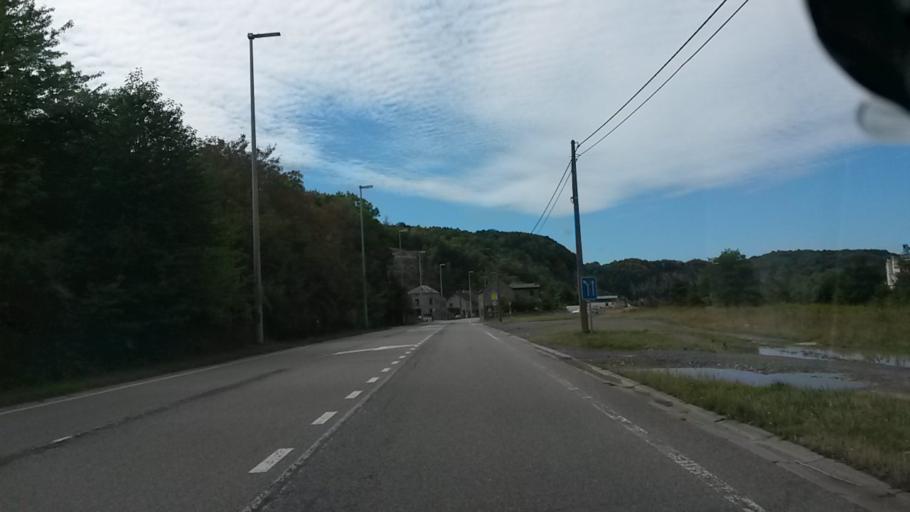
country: BE
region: Wallonia
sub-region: Province de Namur
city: Andenne
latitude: 50.4772
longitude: 5.0143
